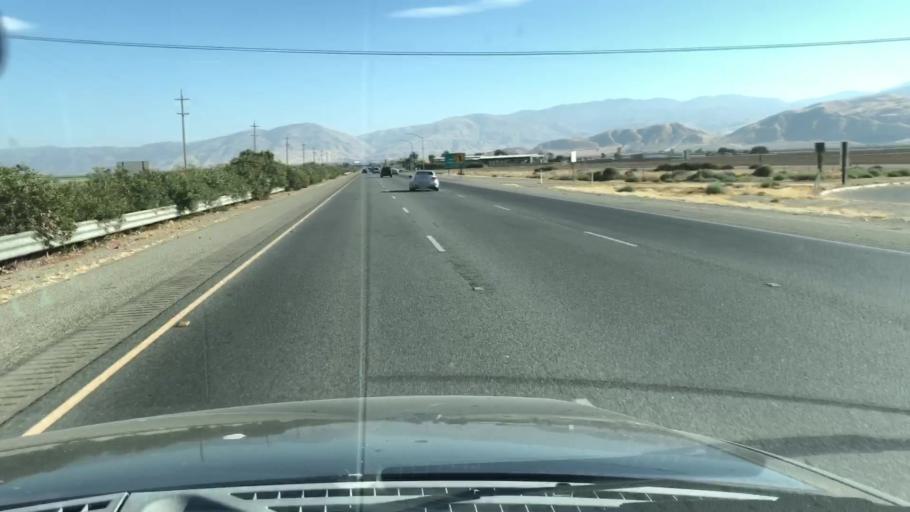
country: US
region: California
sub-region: Kern County
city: Weedpatch
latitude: 35.0766
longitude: -118.9739
